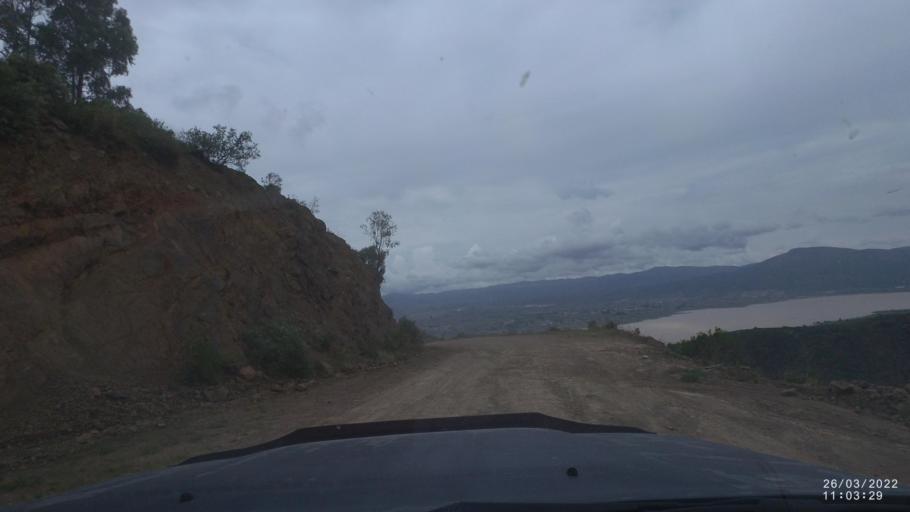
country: BO
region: Cochabamba
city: Tarata
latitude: -17.5273
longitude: -66.0253
